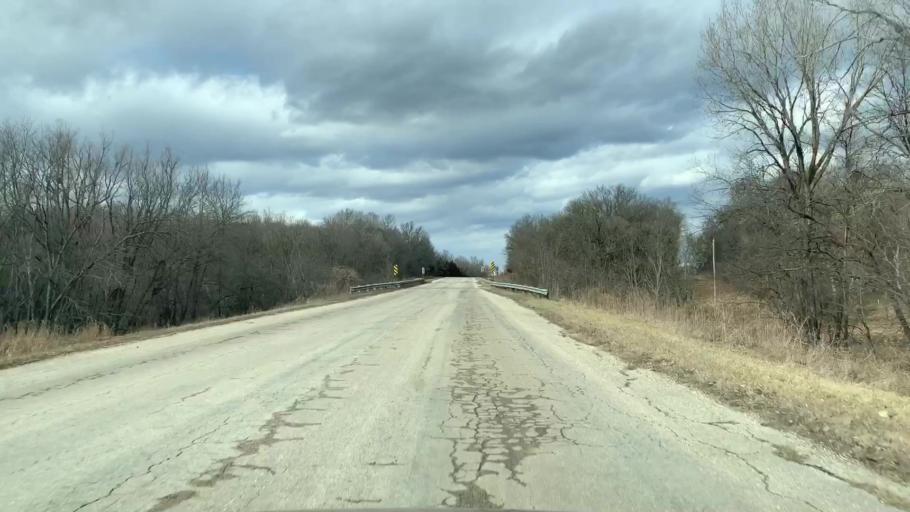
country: US
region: Kansas
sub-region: Allen County
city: Humboldt
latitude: 37.7524
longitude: -95.4709
